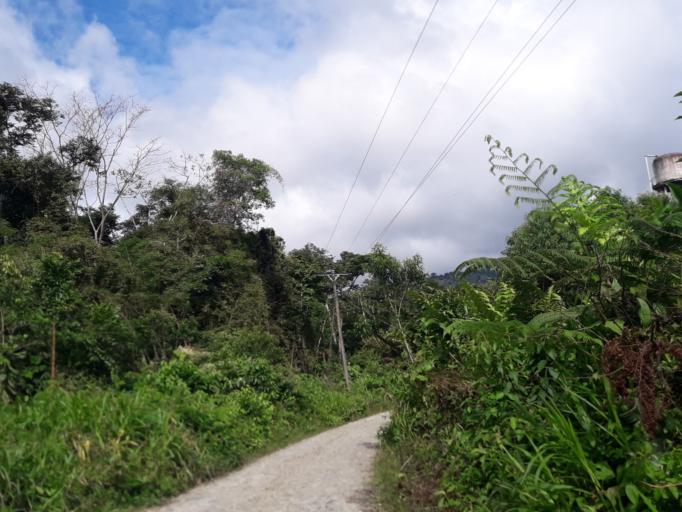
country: EC
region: Napo
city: Archidona
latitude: -0.9428
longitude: -77.8834
